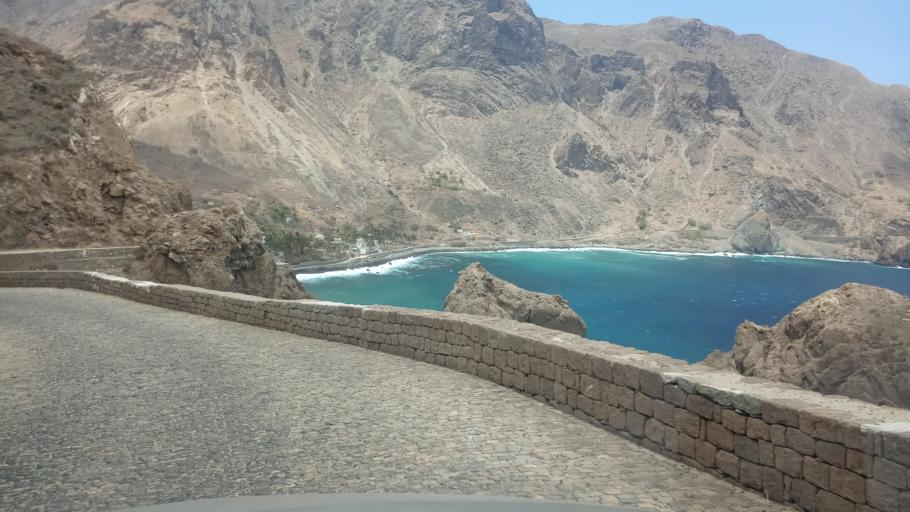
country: CV
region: Brava
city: Vila Nova Sintra
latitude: 14.8768
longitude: -24.7335
